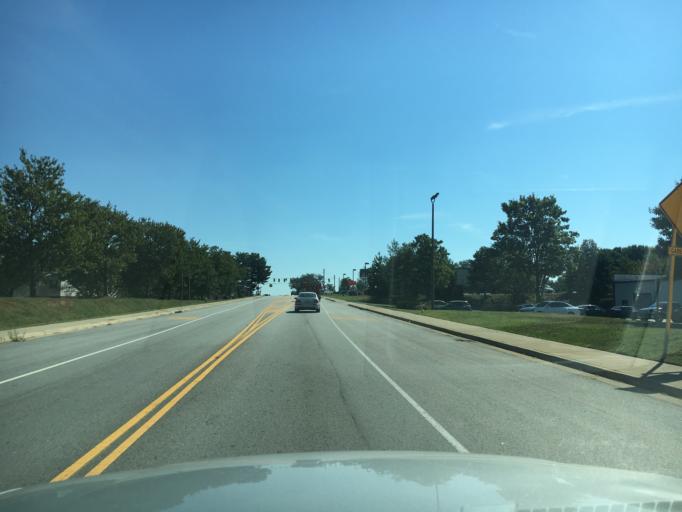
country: US
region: South Carolina
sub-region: Greenville County
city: Five Forks
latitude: 34.8367
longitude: -82.2832
